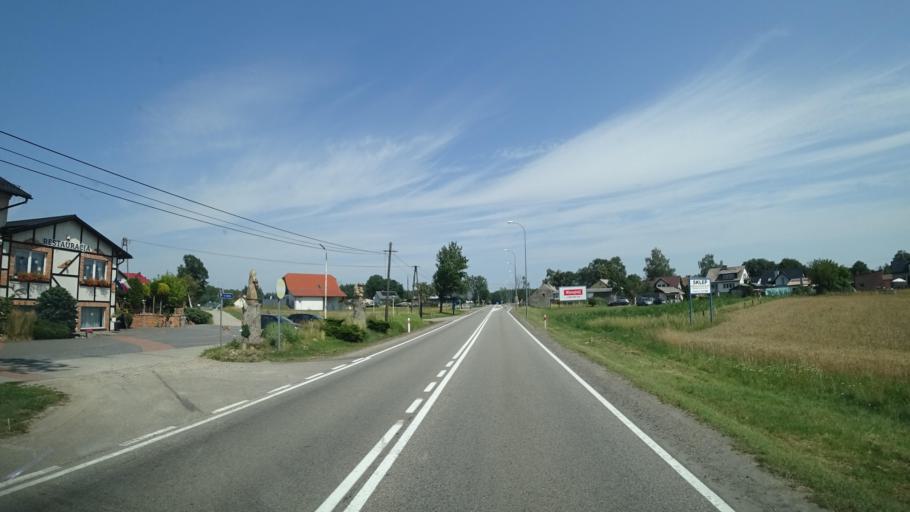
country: PL
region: Pomeranian Voivodeship
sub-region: Powiat koscierski
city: Grabowo Koscierskie
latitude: 54.1845
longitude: 18.0977
